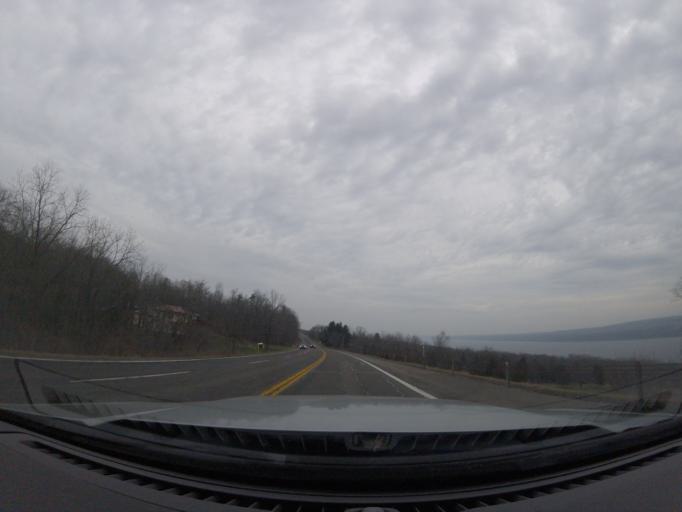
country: US
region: New York
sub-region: Yates County
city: Dundee
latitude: 42.5295
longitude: -76.9176
